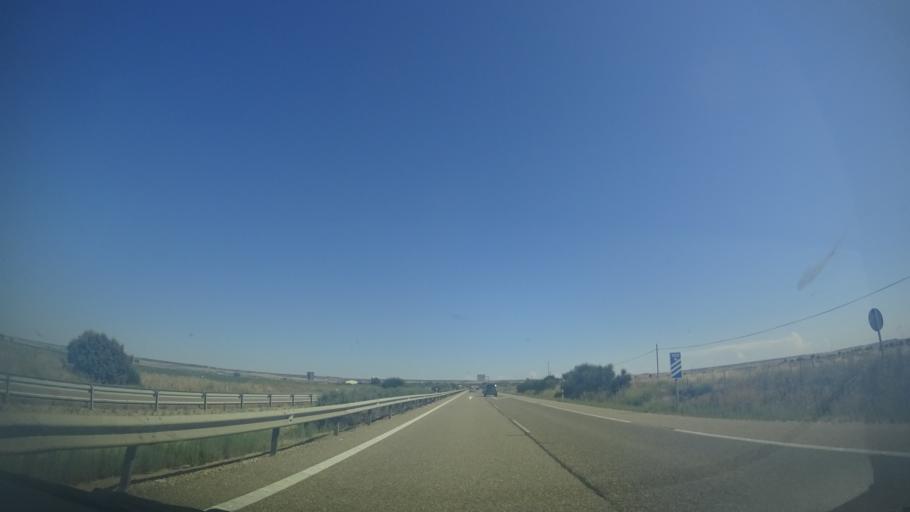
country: ES
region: Castille and Leon
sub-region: Provincia de Valladolid
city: San Pedro de Latarce
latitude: 41.7727
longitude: -5.3090
